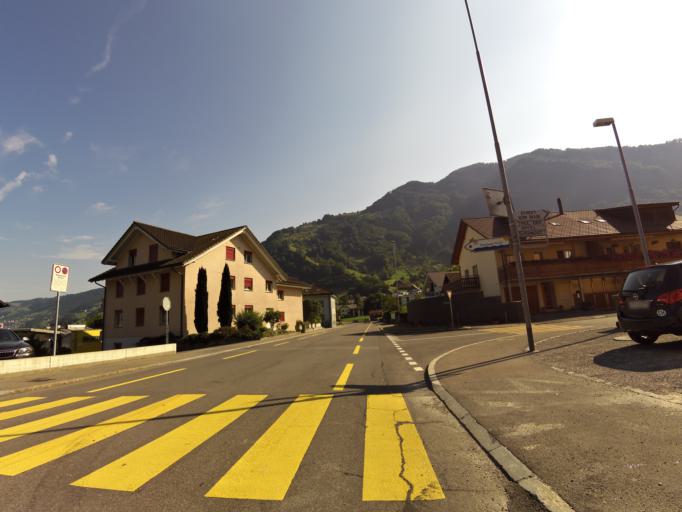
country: CH
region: Schwyz
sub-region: Bezirk Schwyz
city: Arth
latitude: 47.0681
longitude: 8.5261
